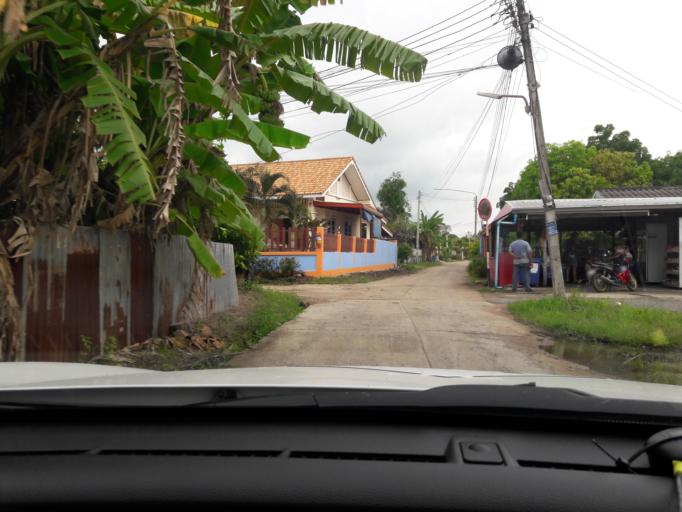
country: TH
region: Nakhon Sawan
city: Tak Fa
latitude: 15.3459
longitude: 100.5018
